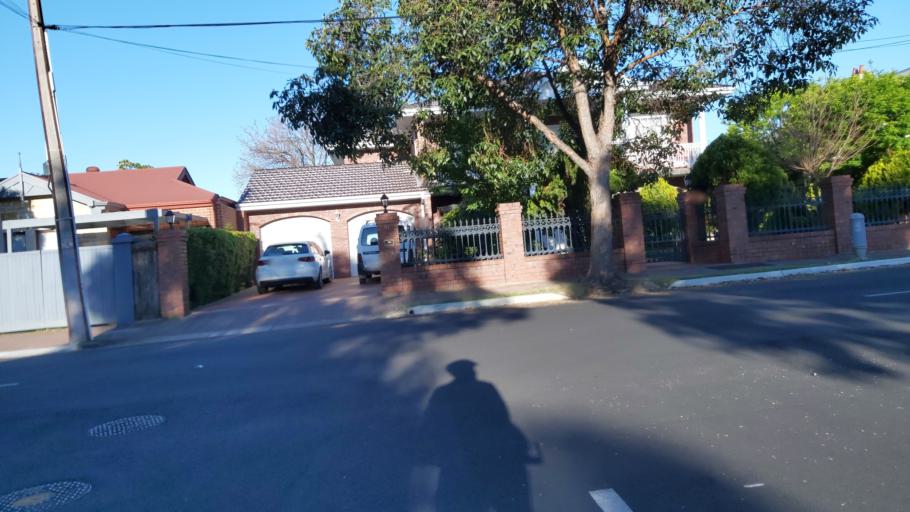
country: AU
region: South Australia
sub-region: Unley
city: Fullarton
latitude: -34.9494
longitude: 138.6213
